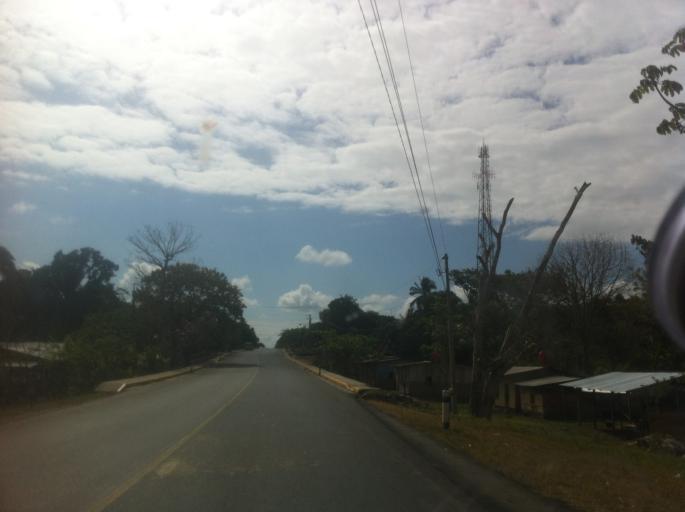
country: NI
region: Rio San Juan
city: San Carlos
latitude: 11.2868
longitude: -84.7215
